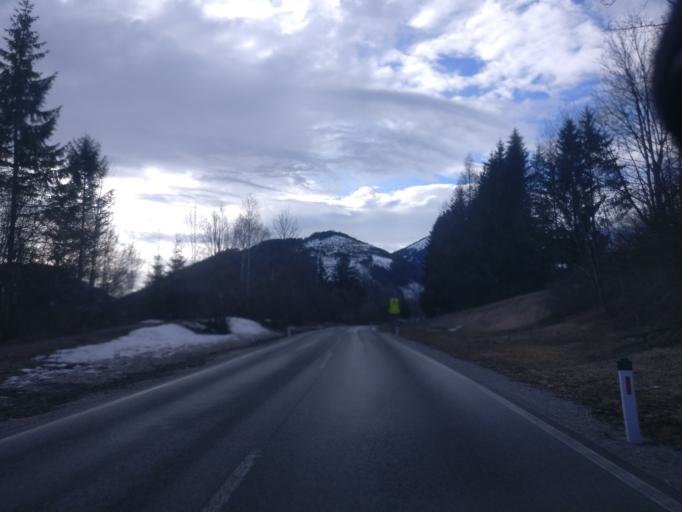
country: AT
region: Styria
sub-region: Politischer Bezirk Liezen
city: Hall bei Admont
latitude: 47.5916
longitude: 14.4754
